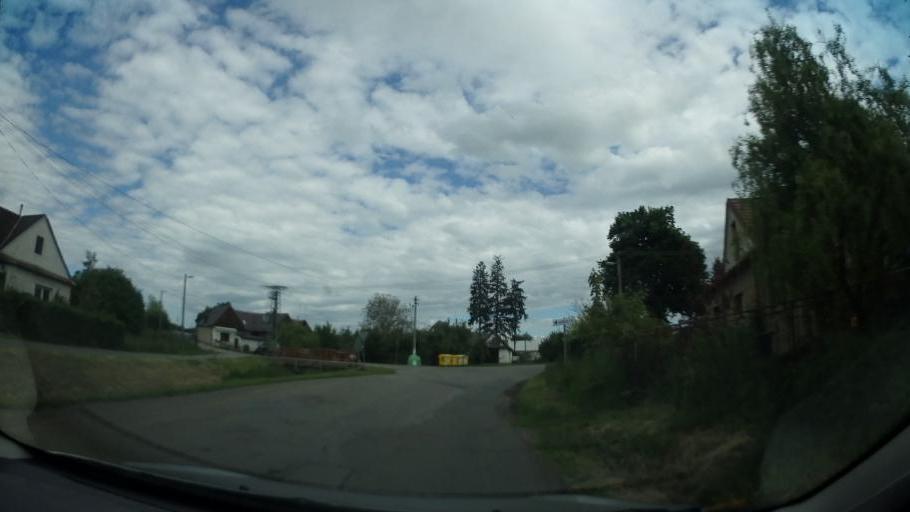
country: CZ
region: Pardubicky
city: Kuncina
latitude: 49.8388
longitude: 16.6982
